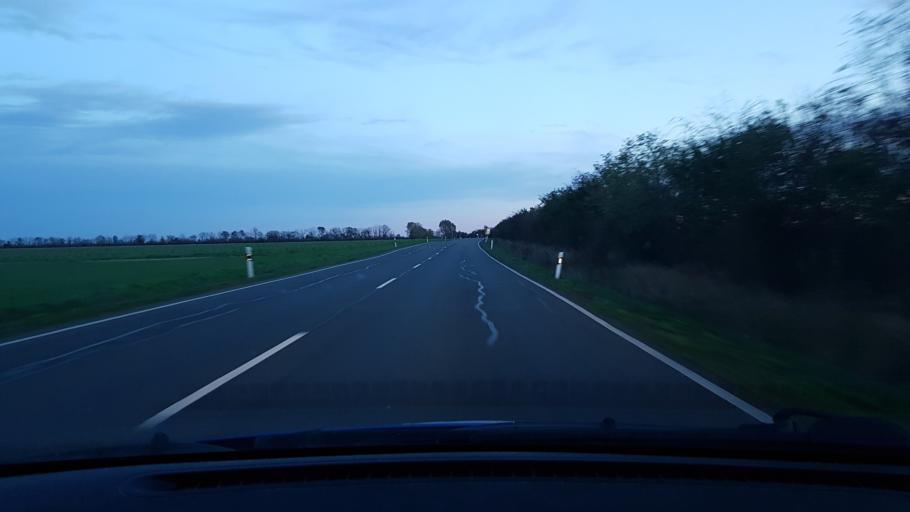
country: DE
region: Saxony-Anhalt
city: Zerbst
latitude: 51.9960
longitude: 12.0374
